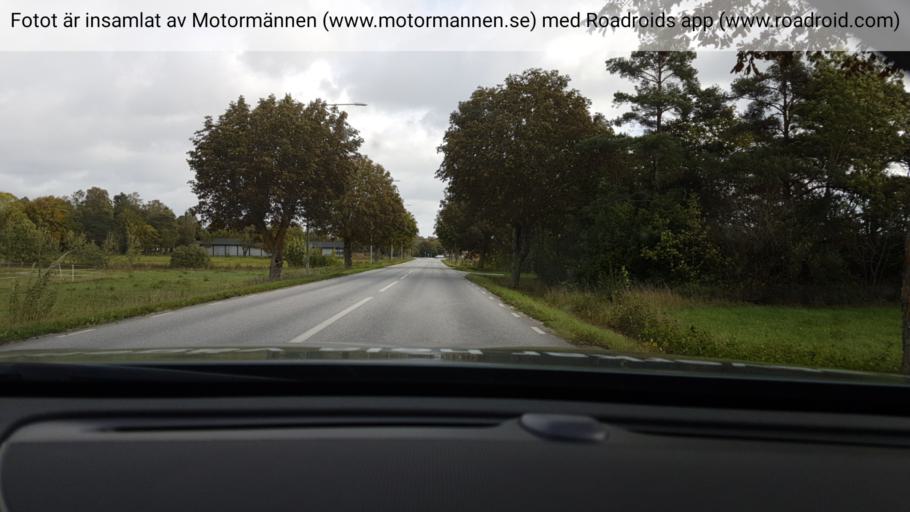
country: SE
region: Gotland
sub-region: Gotland
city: Slite
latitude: 57.7813
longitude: 18.7825
